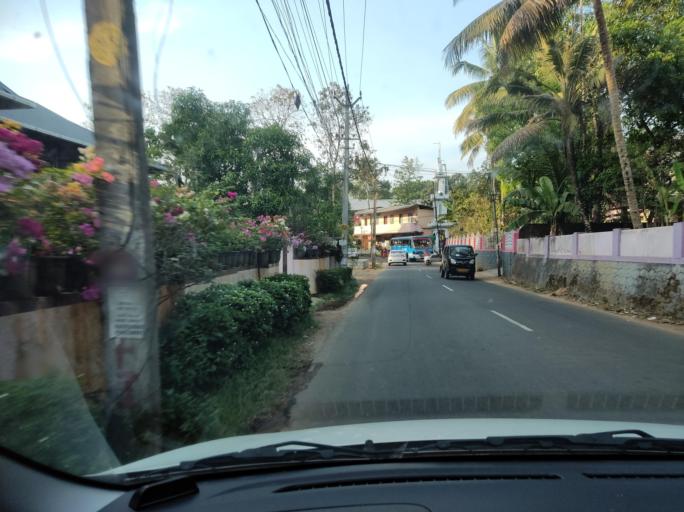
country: IN
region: Kerala
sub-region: Kottayam
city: Kottayam
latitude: 9.6849
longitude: 76.5056
